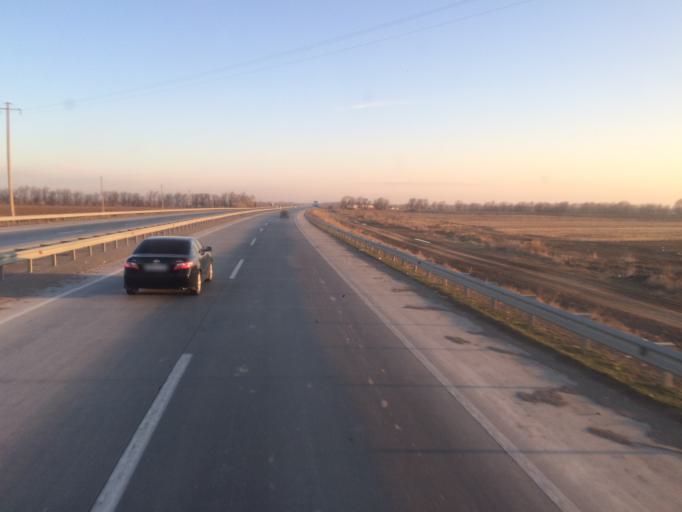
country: KZ
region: Ongtustik Qazaqstan
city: Turkestan
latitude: 43.2092
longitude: 68.4791
